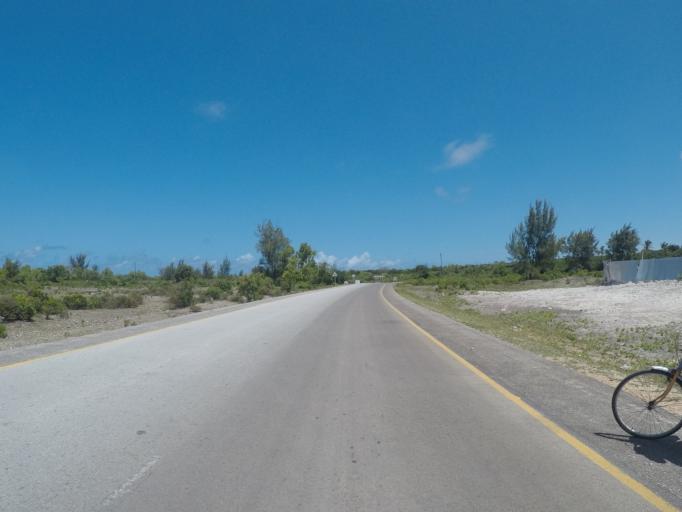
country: TZ
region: Zanzibar Central/South
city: Nganane
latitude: -6.4094
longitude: 39.5640
